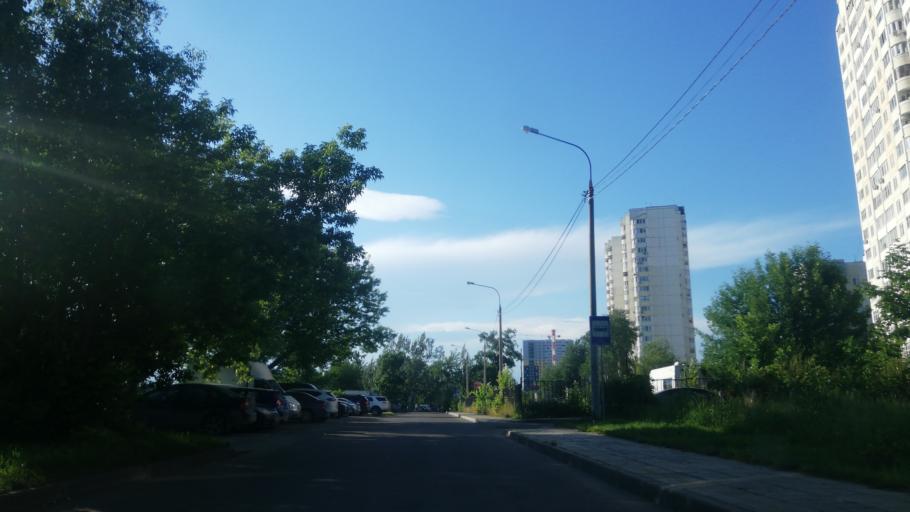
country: RU
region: Moskovskaya
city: Dolgoprudnyy
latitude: 55.9401
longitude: 37.4860
